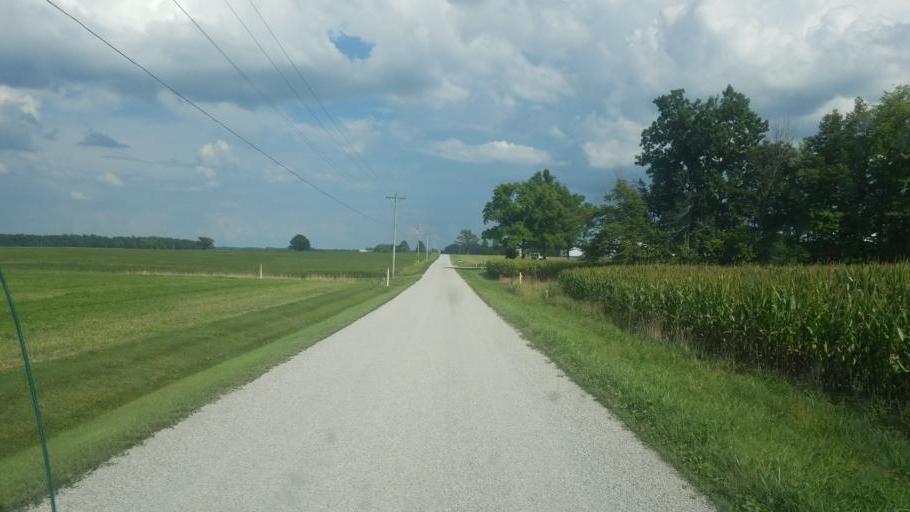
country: US
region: Ohio
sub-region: Huron County
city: Willard
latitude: 40.9966
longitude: -82.8263
